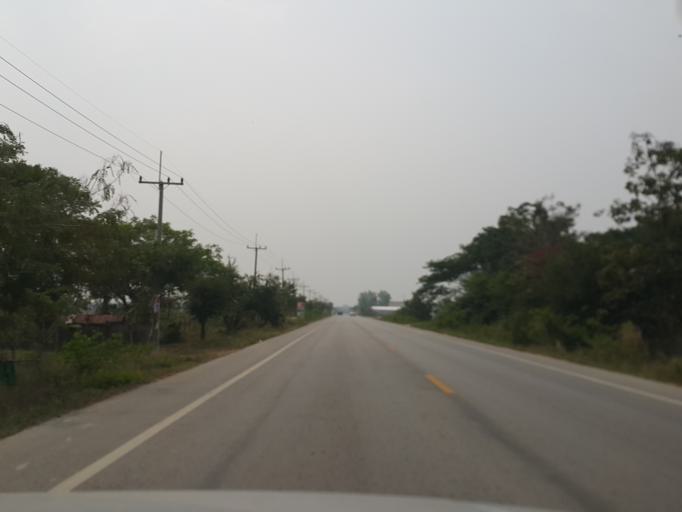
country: TH
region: Lampang
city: Ko Kha
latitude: 18.2178
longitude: 99.3951
